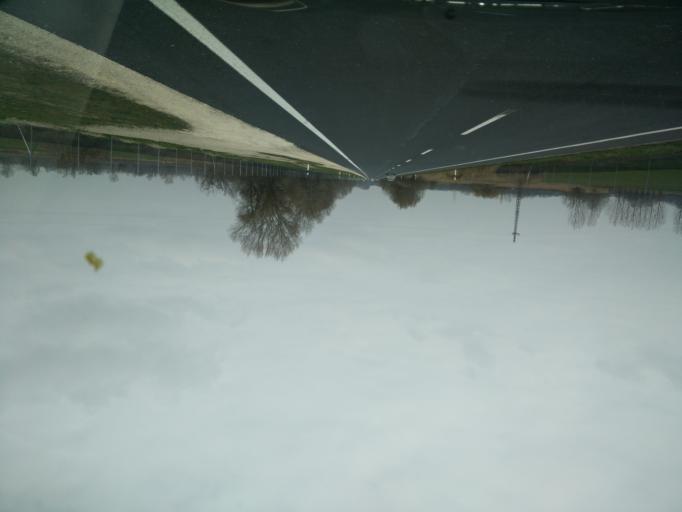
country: HU
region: Gyor-Moson-Sopron
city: Toltestava
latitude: 47.6999
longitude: 17.7714
